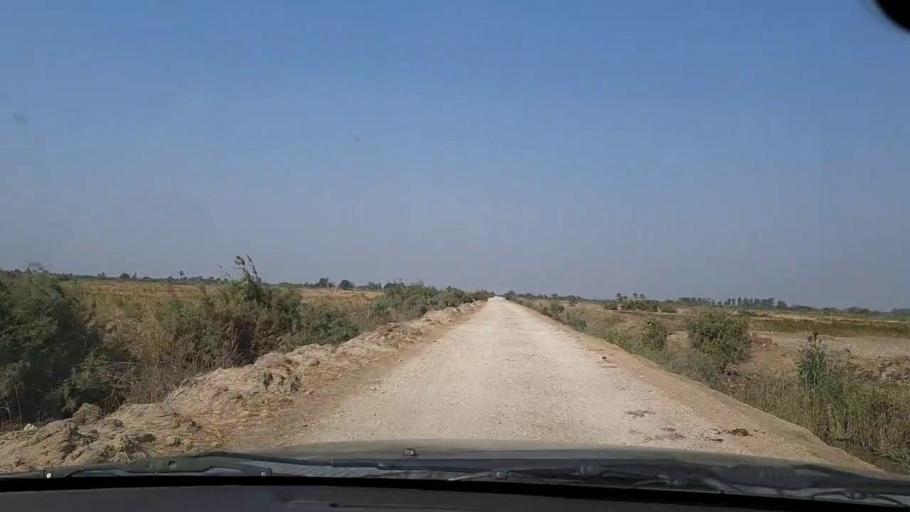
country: PK
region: Sindh
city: Mirpur Sakro
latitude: 24.3698
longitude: 67.6830
